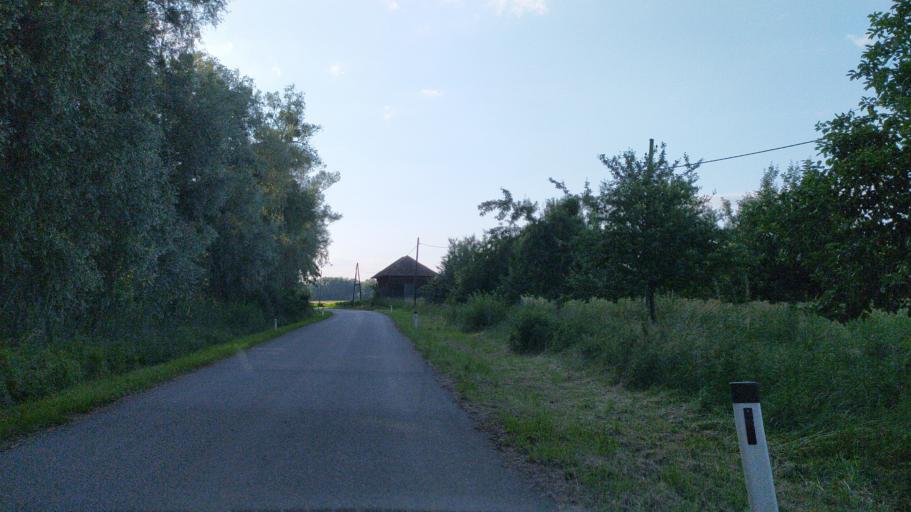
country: AT
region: Lower Austria
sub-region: Politischer Bezirk Amstetten
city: Strengberg
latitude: 48.1804
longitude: 14.6157
